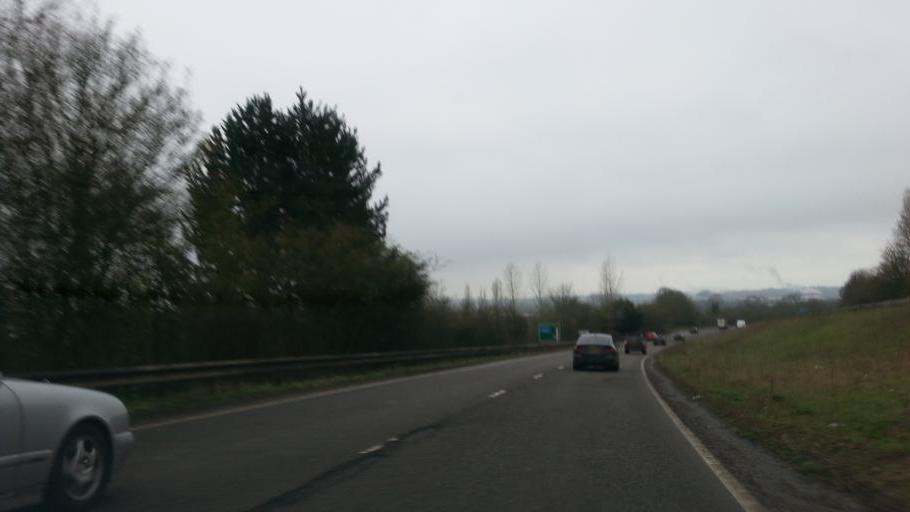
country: GB
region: England
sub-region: Oxfordshire
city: Banbury
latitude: 52.0706
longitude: -1.3002
